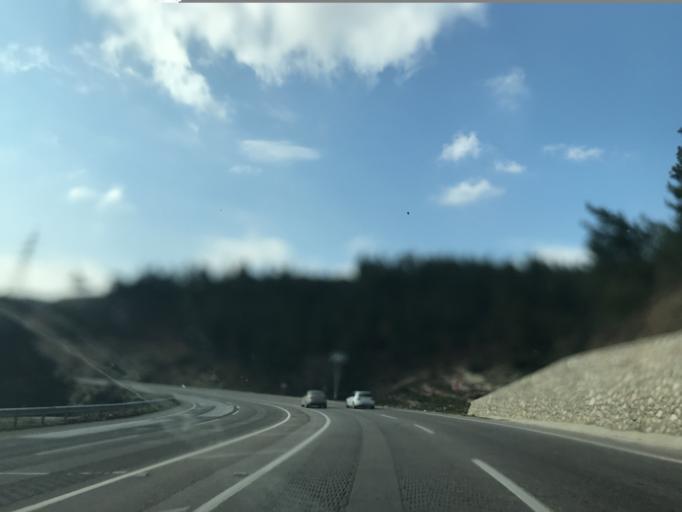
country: TR
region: Hatay
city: Belen
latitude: 36.4812
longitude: 36.2415
